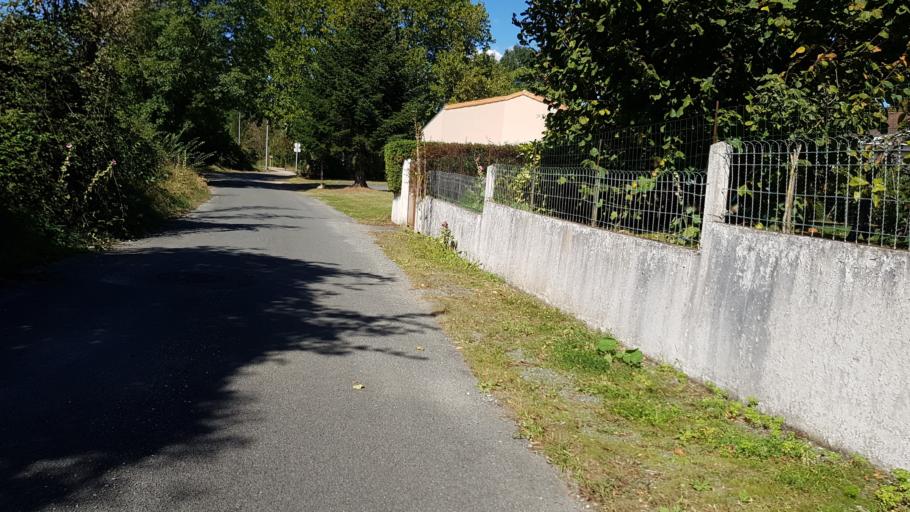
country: FR
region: Poitou-Charentes
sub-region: Departement des Deux-Sevres
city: Vouille
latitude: 46.3169
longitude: -0.3692
